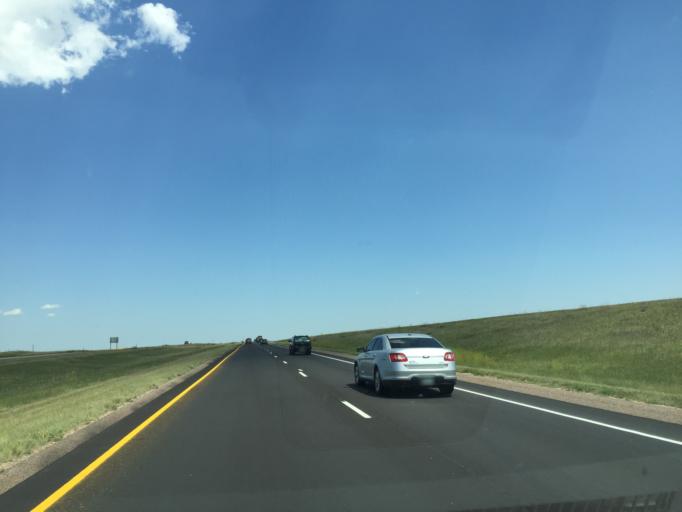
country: US
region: Colorado
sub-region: Lincoln County
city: Hugo
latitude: 39.2797
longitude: -103.3785
